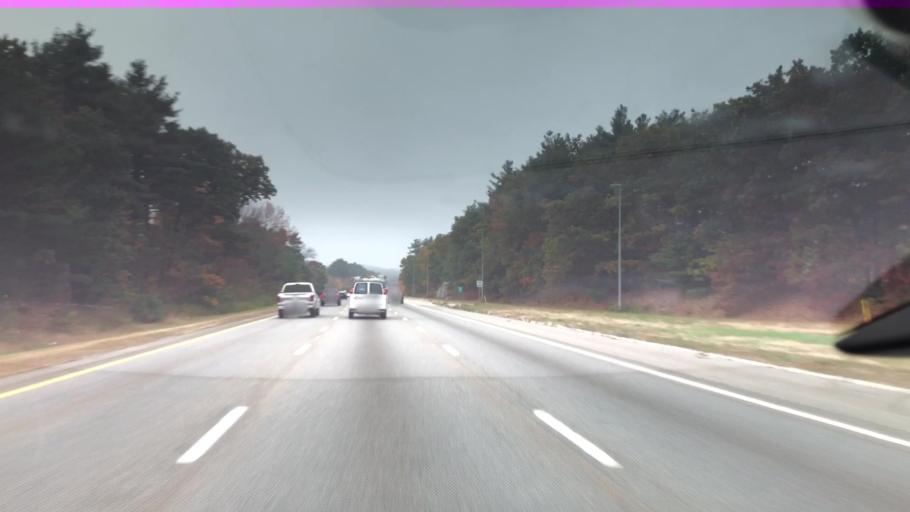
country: US
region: Massachusetts
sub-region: Worcester County
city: Harvard
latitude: 42.4850
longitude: -71.5466
